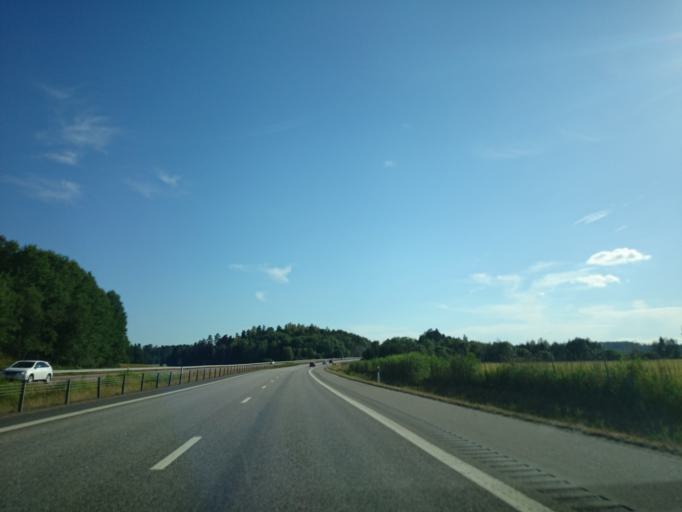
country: SE
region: Soedermanland
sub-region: Gnesta Kommun
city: Gnesta
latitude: 58.8892
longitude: 17.2618
